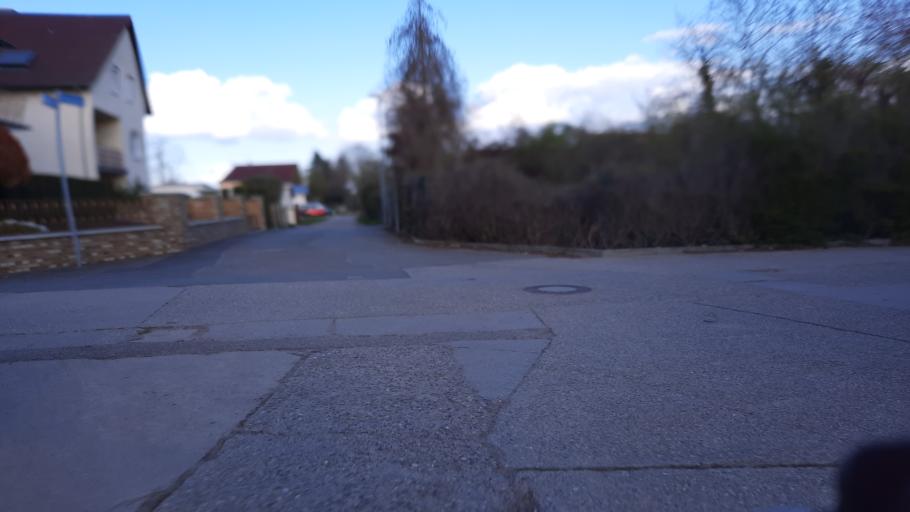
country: DE
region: Rheinland-Pfalz
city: Offstein
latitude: 49.6076
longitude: 8.2628
